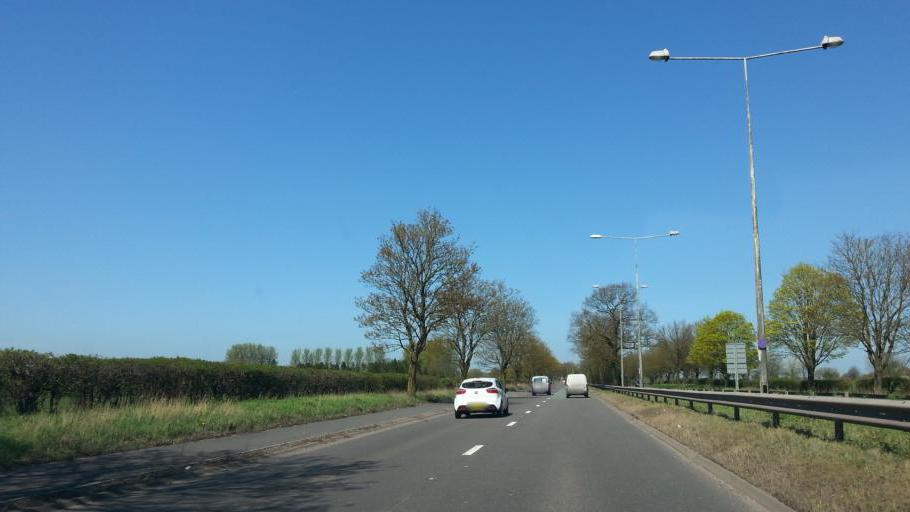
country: GB
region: England
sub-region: Staffordshire
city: Brewood
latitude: 52.6753
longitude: -2.1306
